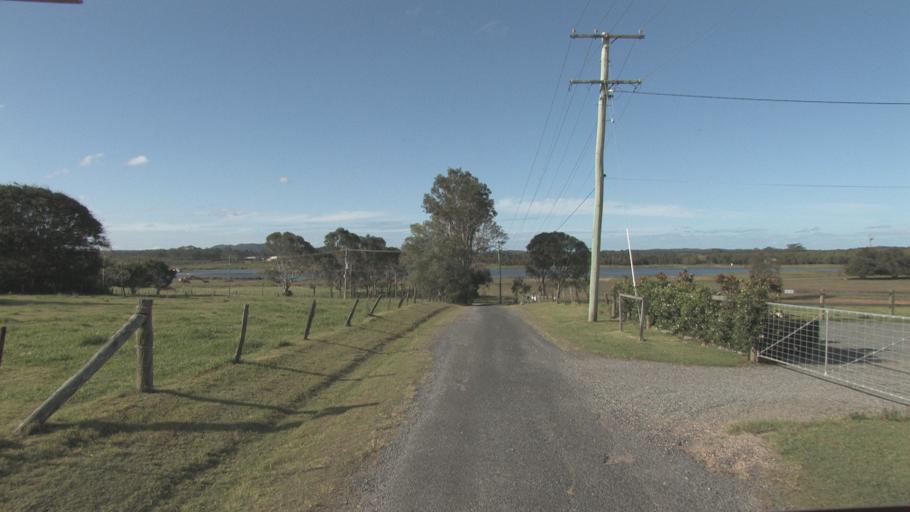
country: AU
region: Queensland
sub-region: Gold Coast
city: Yatala
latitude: -27.6934
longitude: 153.2374
